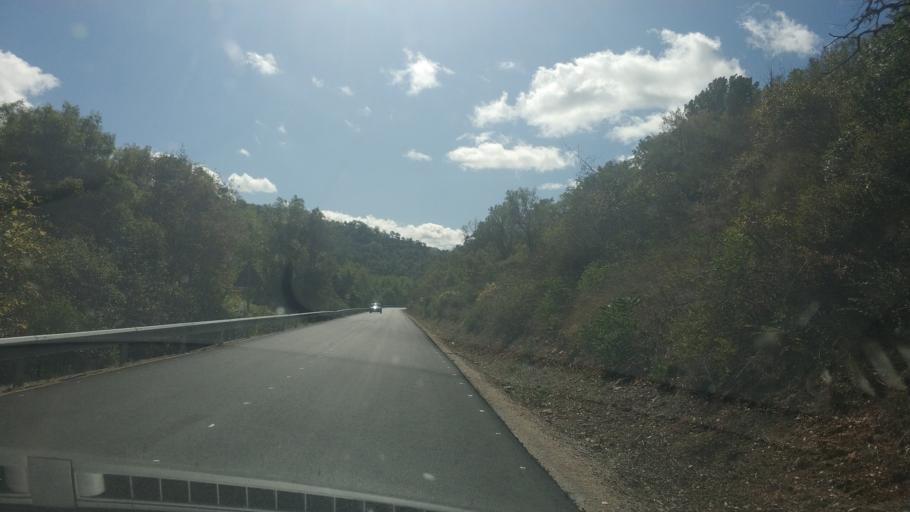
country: ES
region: Castille and Leon
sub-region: Provincia de Burgos
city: Covarrubias
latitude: 42.0536
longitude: -3.5238
